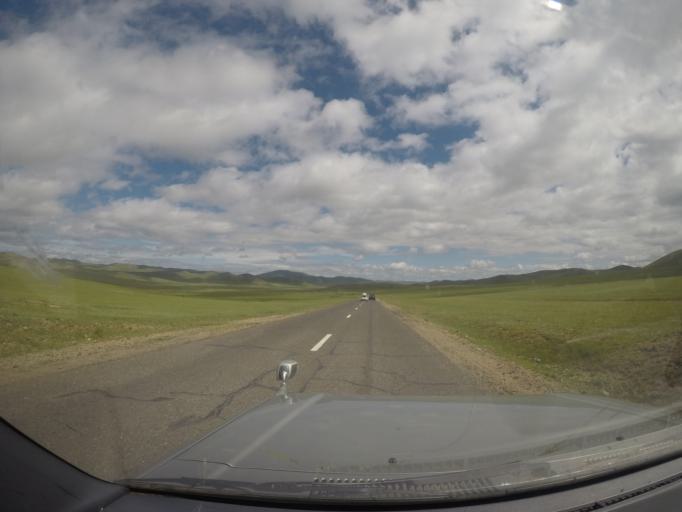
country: MN
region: Hentiy
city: Modot
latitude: 47.7472
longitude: 108.9722
